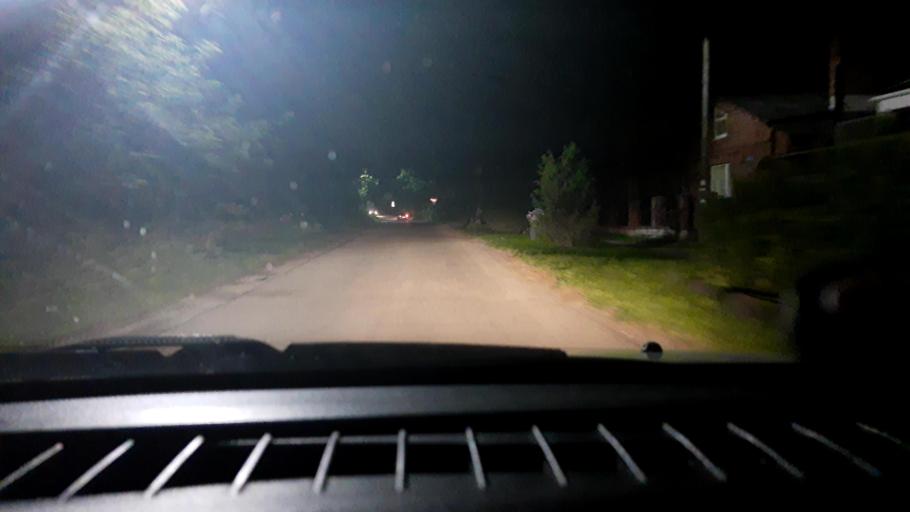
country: RU
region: Nizjnij Novgorod
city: Bogorodsk
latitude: 56.0991
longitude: 43.5275
